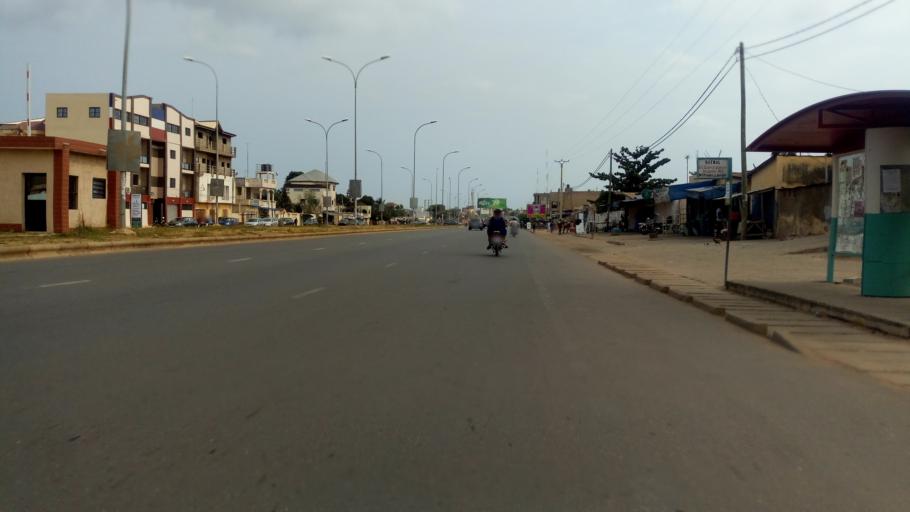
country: TG
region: Maritime
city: Lome
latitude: 6.2049
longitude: 1.1819
